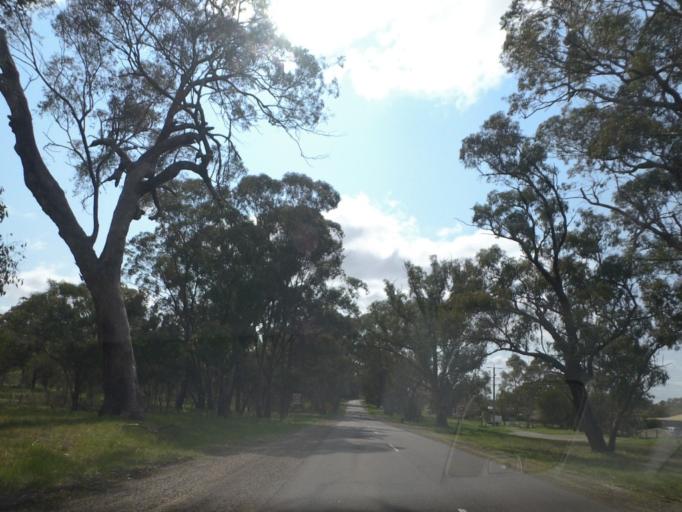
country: AU
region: Victoria
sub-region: Murrindindi
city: Kinglake West
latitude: -37.1044
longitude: 145.0959
